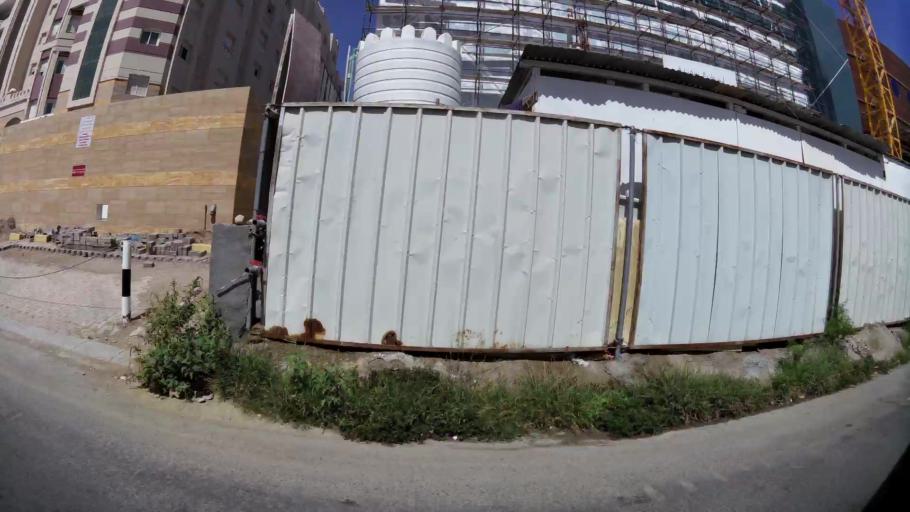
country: OM
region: Muhafazat Masqat
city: Bawshar
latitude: 23.5946
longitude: 58.4037
